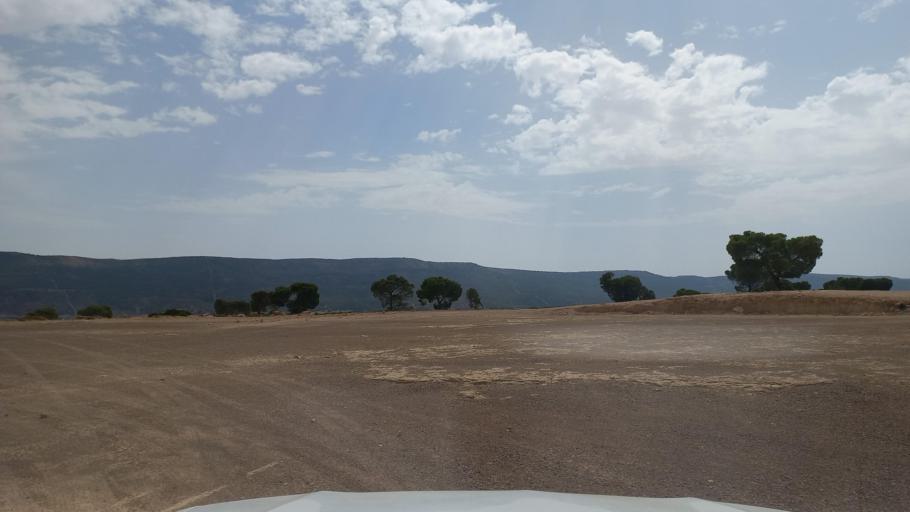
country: TN
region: Al Qasrayn
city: Kasserine
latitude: 35.3770
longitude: 8.8796
